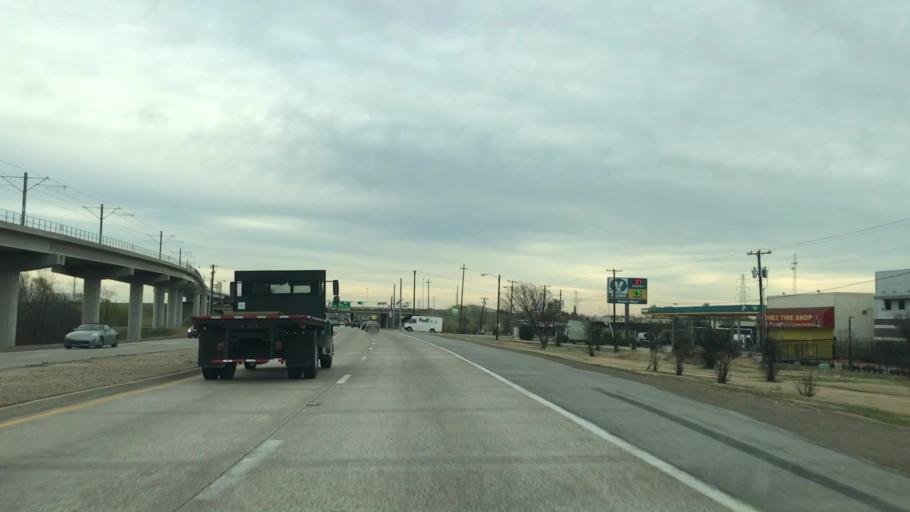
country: US
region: Texas
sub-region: Dallas County
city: Irving
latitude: 32.8518
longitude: -96.8877
